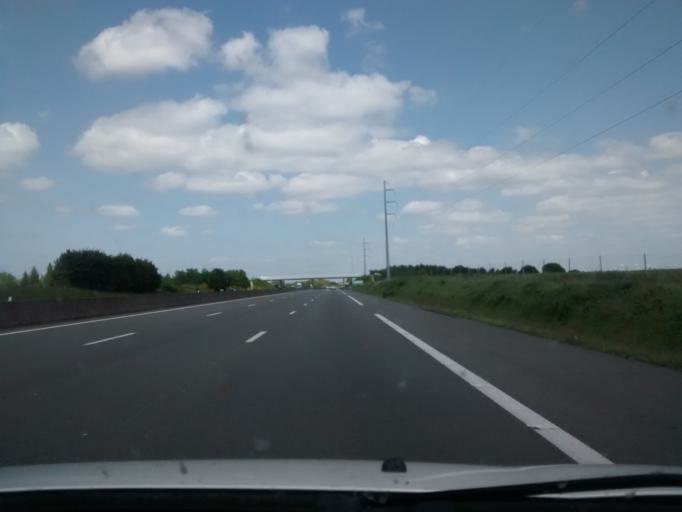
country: FR
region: Centre
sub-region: Departement d'Eure-et-Loir
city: Dammarie
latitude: 48.3556
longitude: 1.4306
